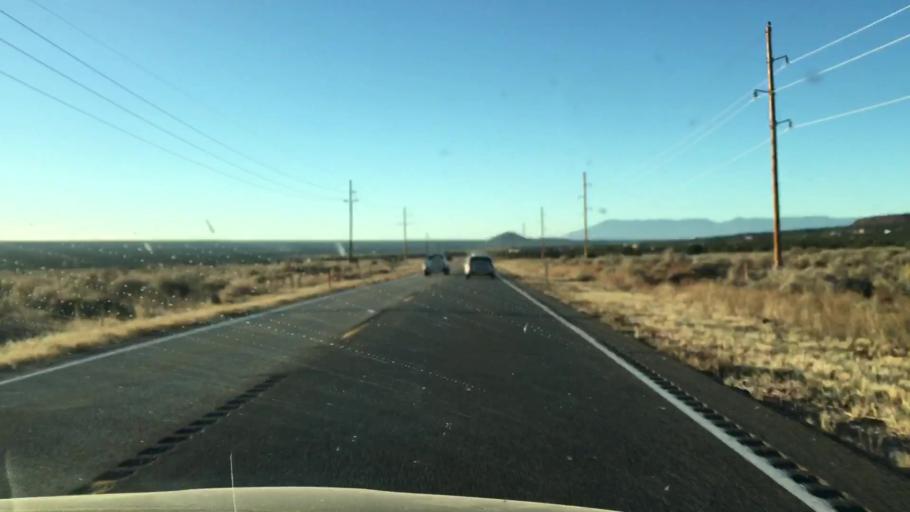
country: US
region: Arizona
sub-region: Mohave County
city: Colorado City
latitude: 37.0287
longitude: -113.0525
